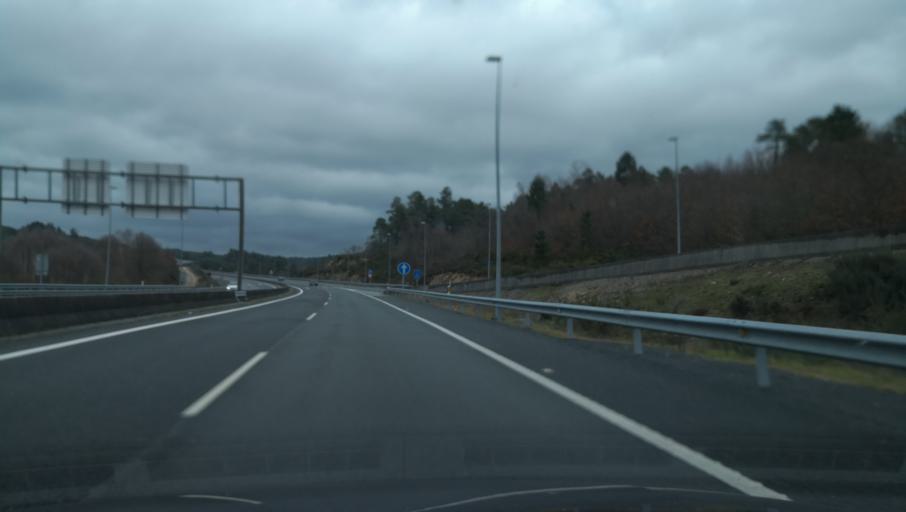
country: ES
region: Galicia
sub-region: Provincia de Ourense
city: Pinor
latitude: 42.5242
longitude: -8.0176
